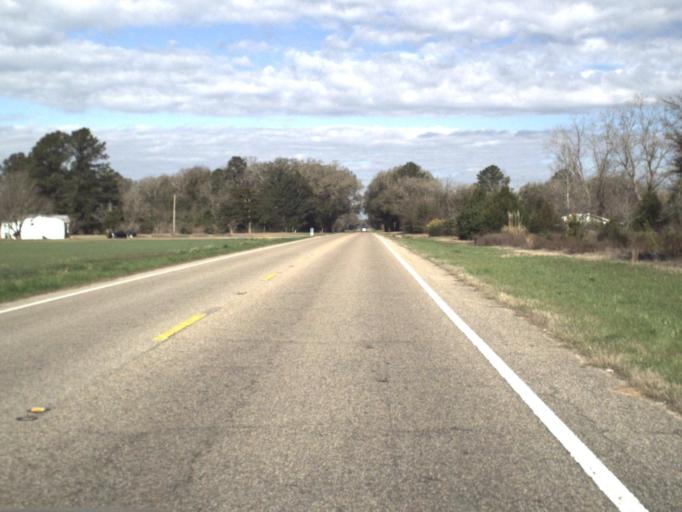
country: US
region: Florida
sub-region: Jackson County
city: Malone
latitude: 30.9812
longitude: -85.1785
